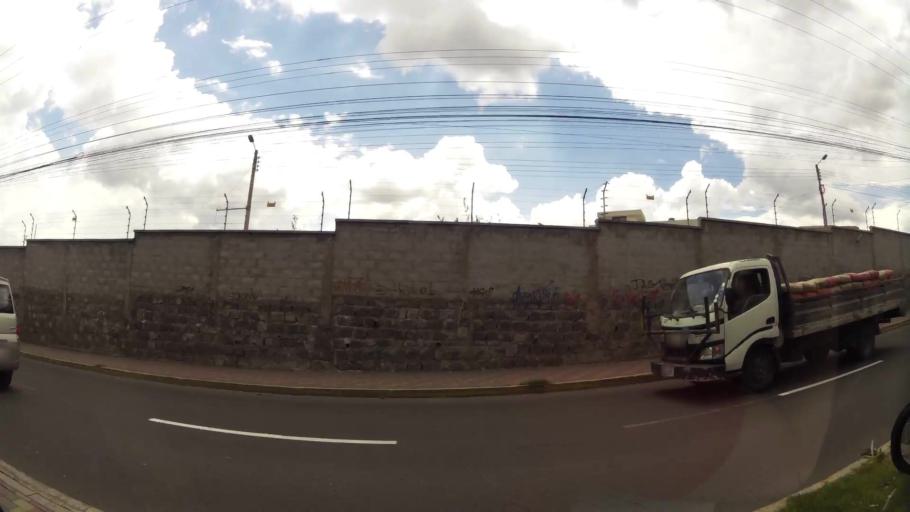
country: EC
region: Pichincha
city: Quito
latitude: -0.0957
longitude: -78.4396
